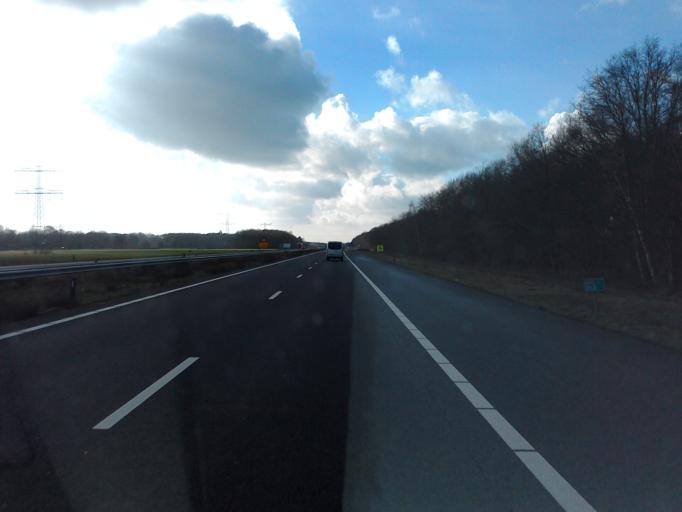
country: NL
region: North Brabant
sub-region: Gemeente Eersel
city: Eersel
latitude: 51.3787
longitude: 5.3378
